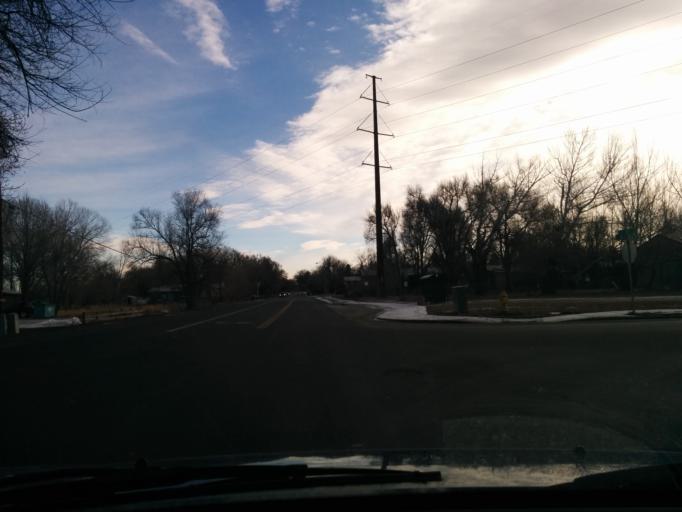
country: US
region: Colorado
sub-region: Larimer County
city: Fort Collins
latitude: 40.5893
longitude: -105.1199
